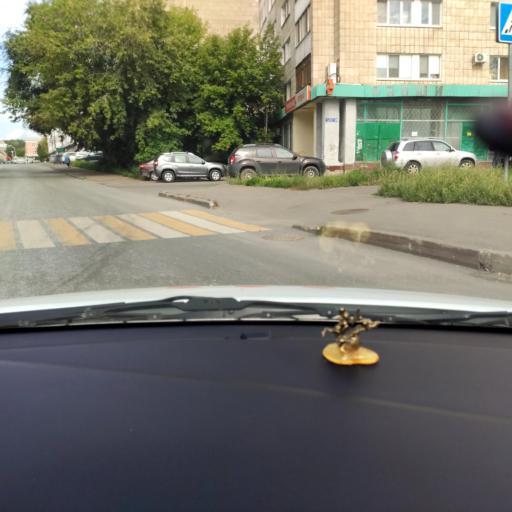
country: RU
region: Tatarstan
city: Osinovo
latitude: 55.8186
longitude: 48.9009
